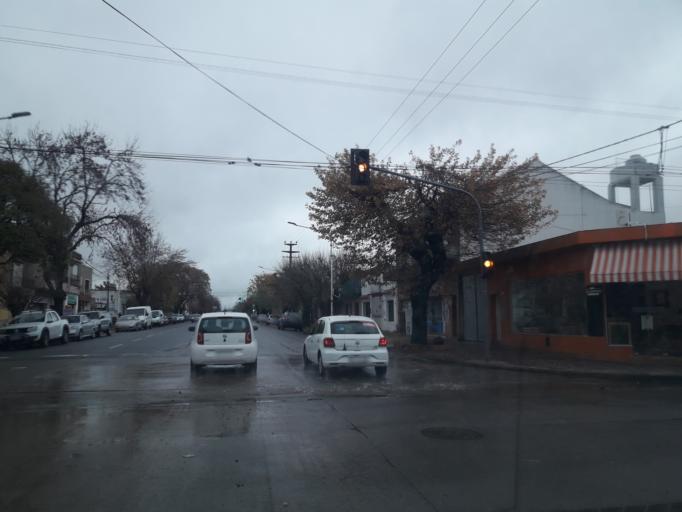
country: AR
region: Buenos Aires
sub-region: Partido de Tandil
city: Tandil
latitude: -37.3247
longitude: -59.1478
